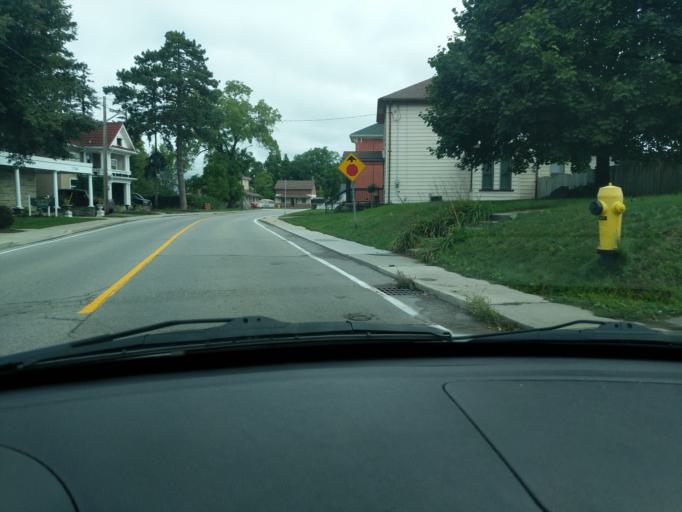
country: CA
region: Ontario
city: Cambridge
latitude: 43.4290
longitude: -80.3096
